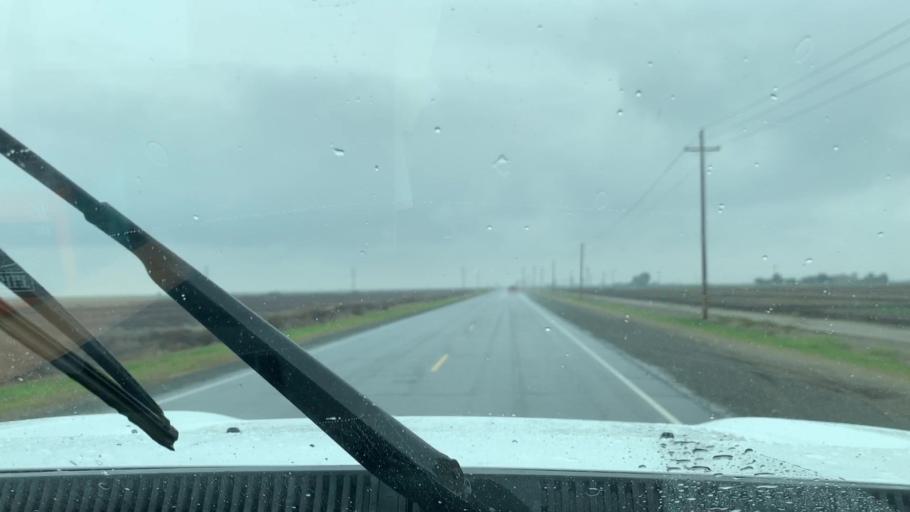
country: US
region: California
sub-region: Tulare County
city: Alpaugh
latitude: 35.9531
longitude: -119.4503
